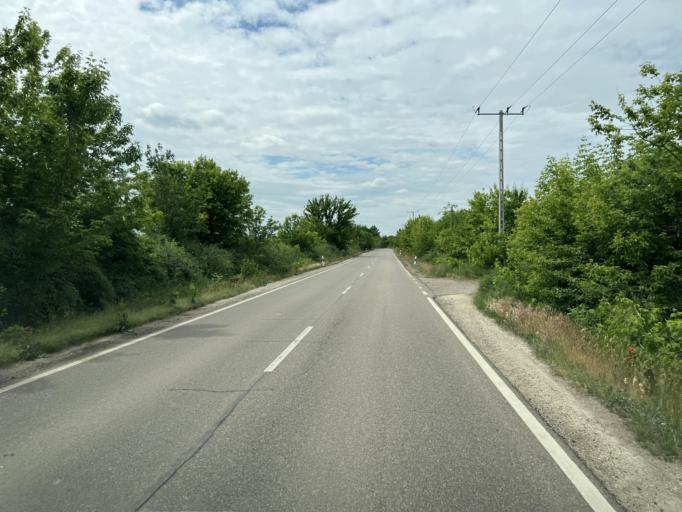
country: HU
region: Pest
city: Koka
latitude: 47.5004
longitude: 19.5881
